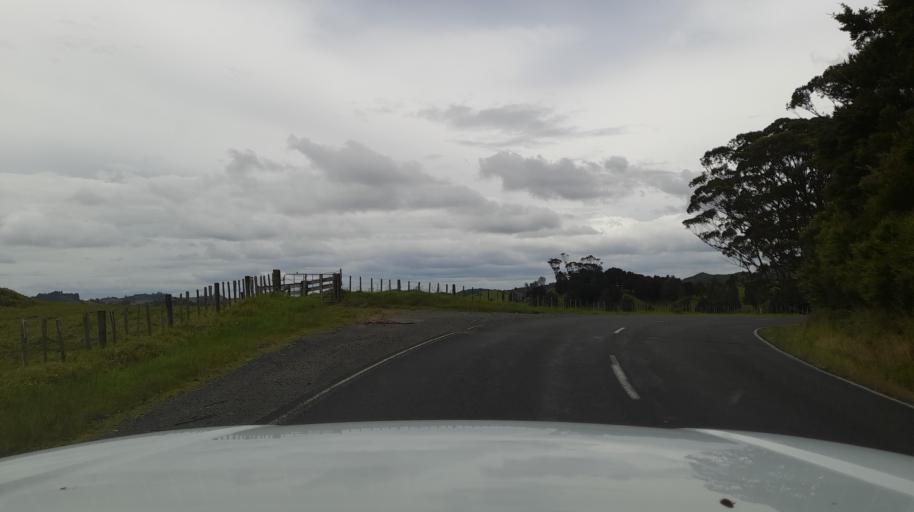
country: NZ
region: Northland
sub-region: Far North District
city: Kaitaia
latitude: -35.2790
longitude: 173.3719
